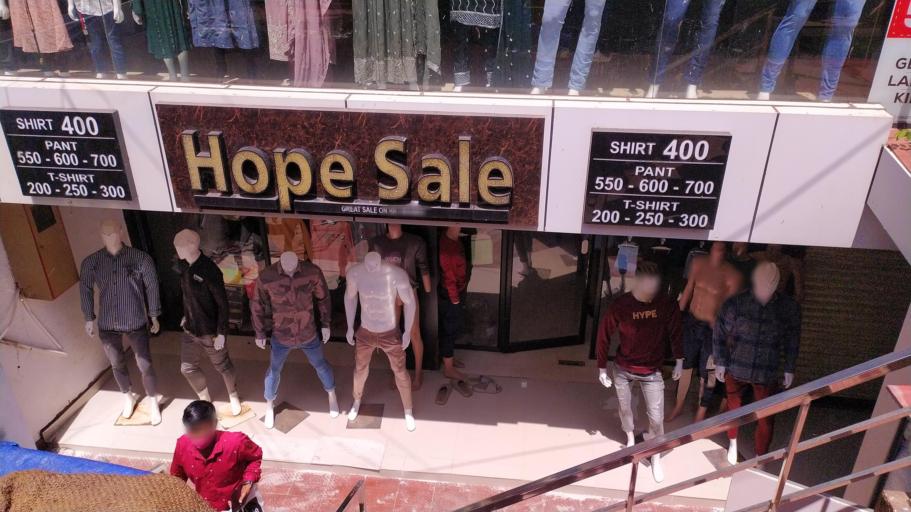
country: IN
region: Kerala
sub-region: Kasaragod District
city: Kannangad
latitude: 12.3233
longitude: 75.0856
